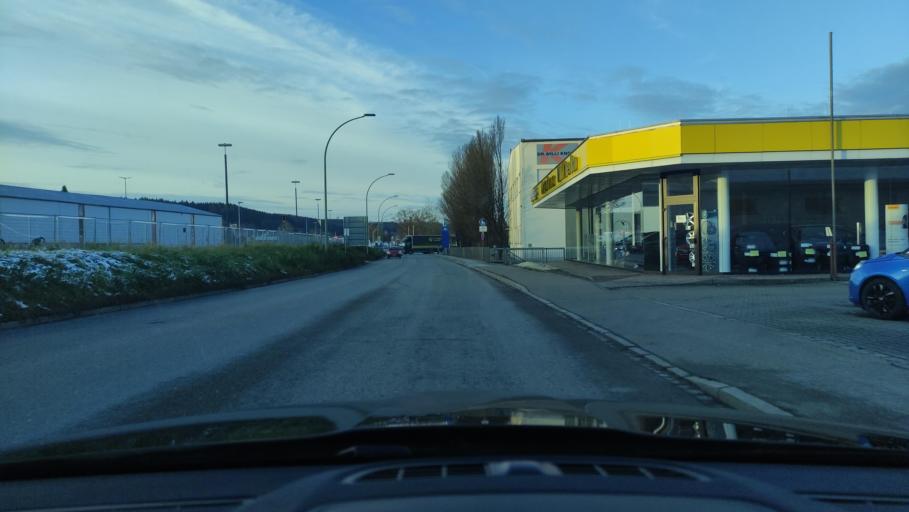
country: DE
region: Bavaria
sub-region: Swabia
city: Krumbach
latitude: 48.2486
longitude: 10.3589
